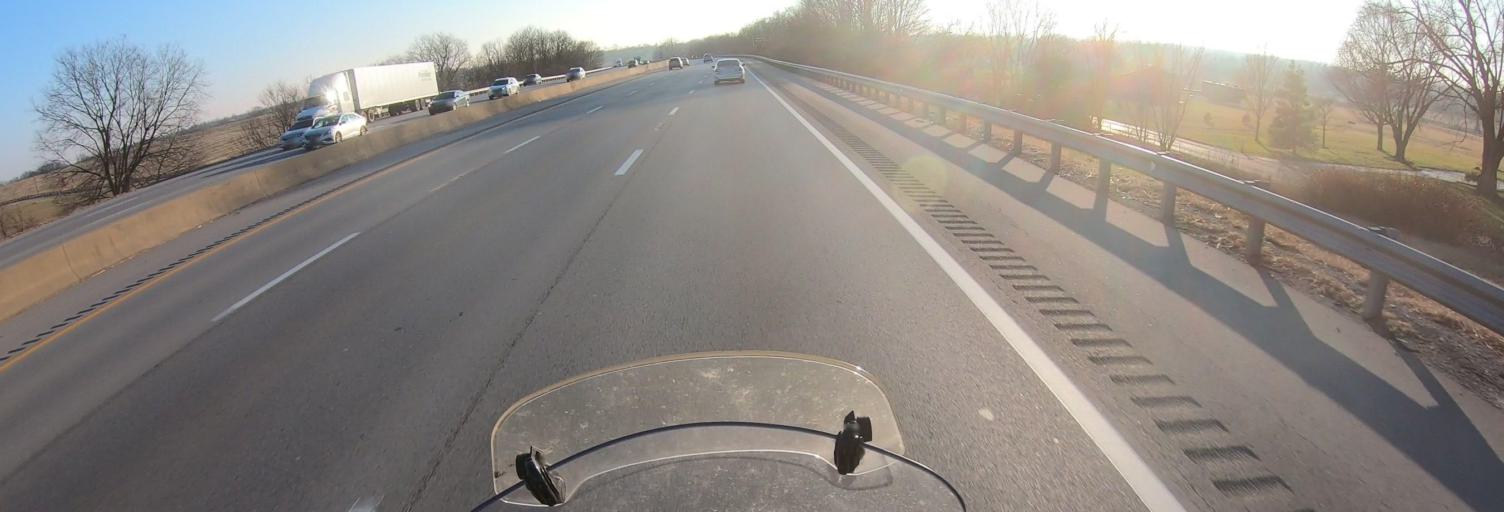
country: US
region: Kentucky
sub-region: Scott County
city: Georgetown
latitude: 38.1734
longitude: -84.5351
